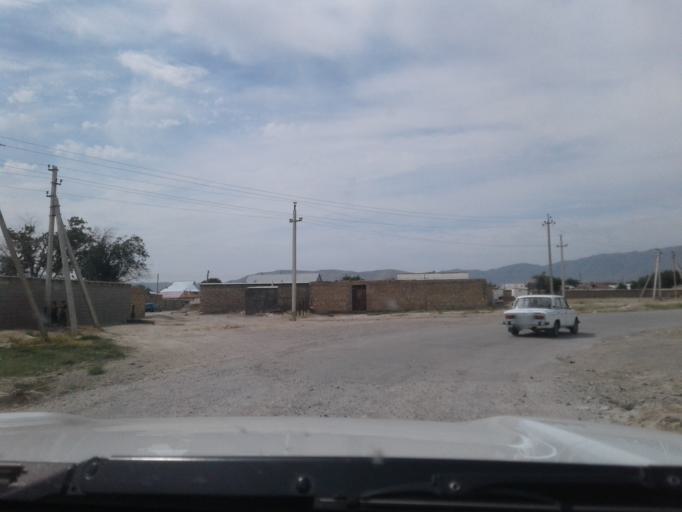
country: TM
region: Balkan
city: Serdar
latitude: 38.9919
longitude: 56.2700
